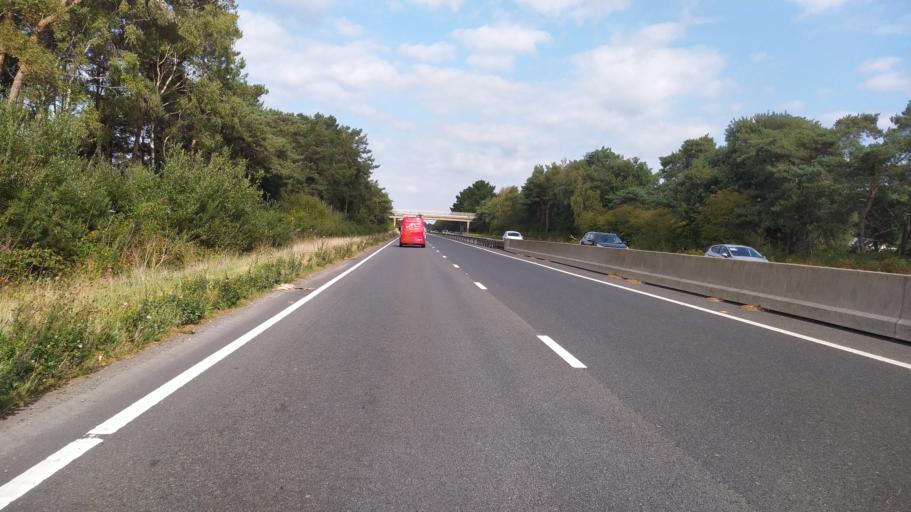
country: GB
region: England
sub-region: Dorset
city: Christchurch
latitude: 50.7750
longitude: -1.8079
